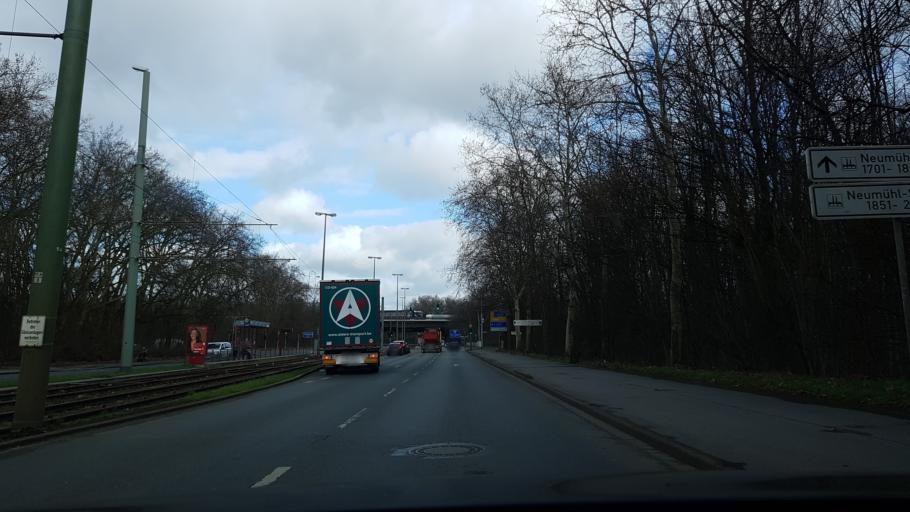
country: DE
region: North Rhine-Westphalia
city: Meiderich
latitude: 51.4824
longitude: 6.7947
